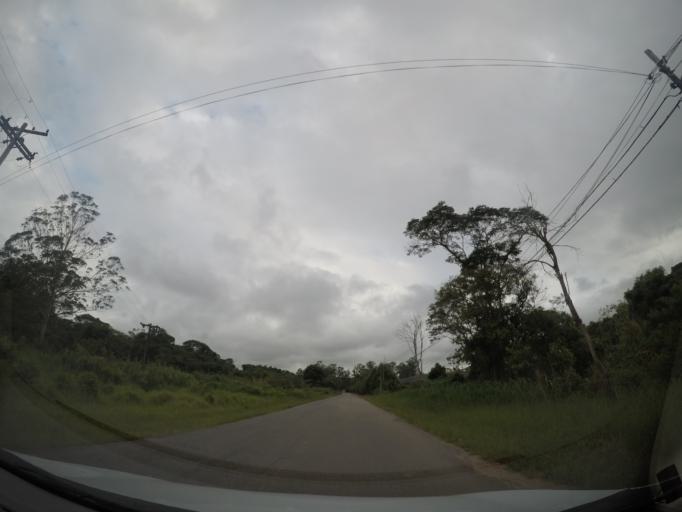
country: BR
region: Sao Paulo
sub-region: Aruja
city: Aruja
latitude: -23.3847
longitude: -46.3571
